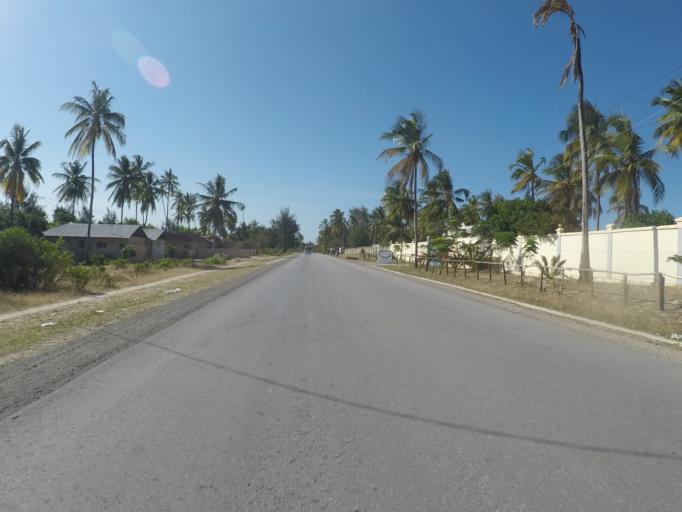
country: TZ
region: Zanzibar Central/South
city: Nganane
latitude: -6.2573
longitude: 39.5325
